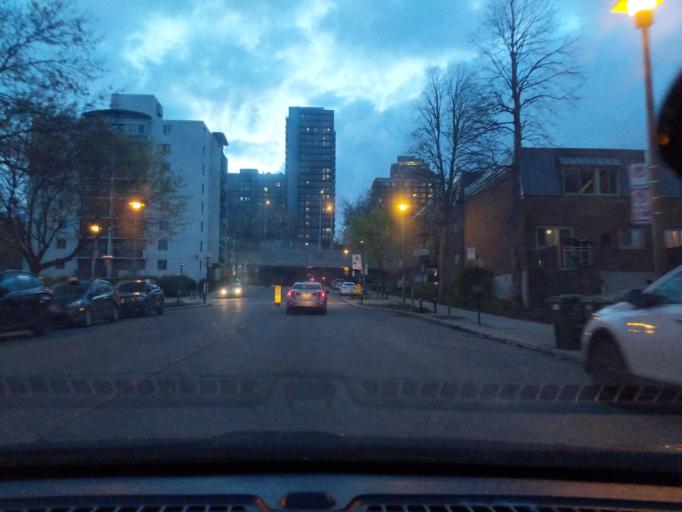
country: CA
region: Quebec
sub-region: Montreal
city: Montreal
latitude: 45.4900
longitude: -73.5735
